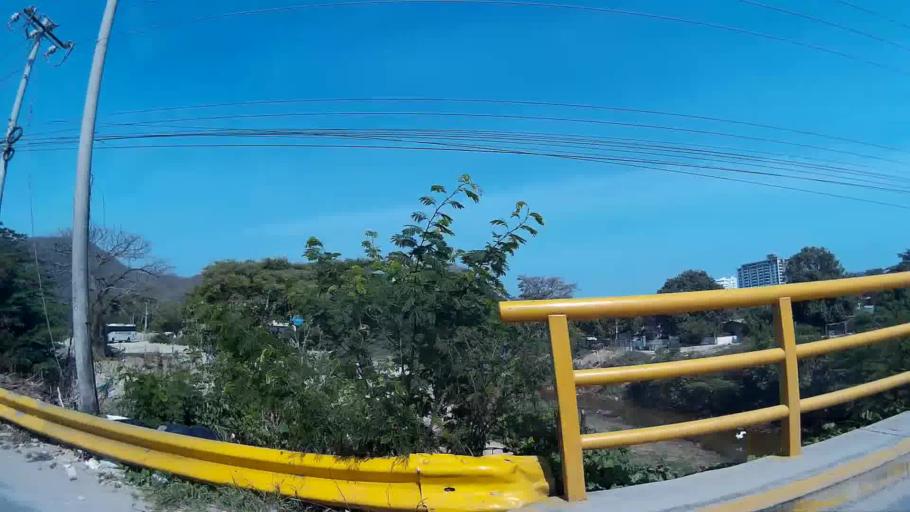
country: CO
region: Magdalena
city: Santa Marta
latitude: 11.1874
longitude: -74.2255
